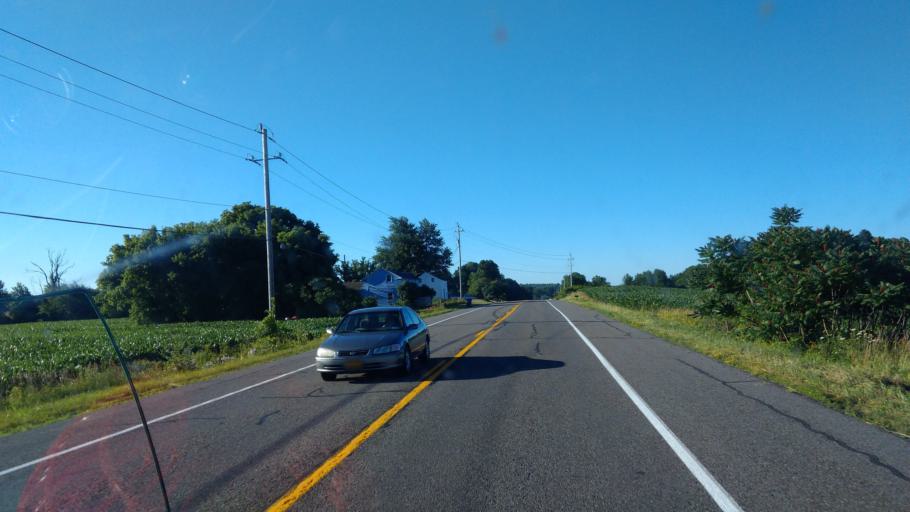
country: US
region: New York
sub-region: Wayne County
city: Lyons
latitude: 43.0063
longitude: -76.9821
